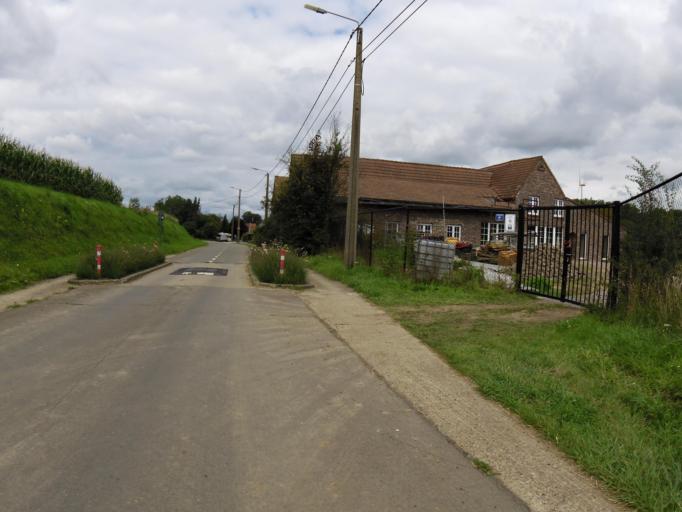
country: BE
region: Flanders
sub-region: Provincie Limburg
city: Tongeren
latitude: 50.7967
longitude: 5.5124
